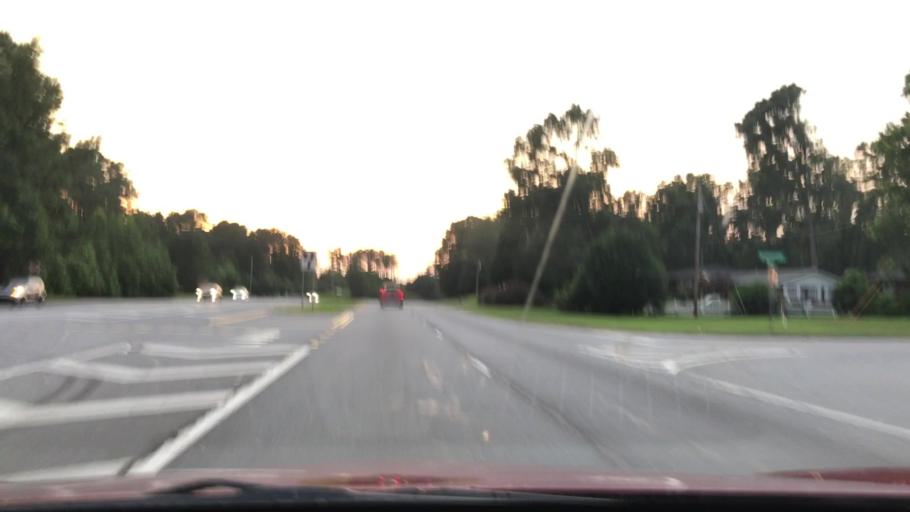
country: US
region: Georgia
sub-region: Gwinnett County
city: Lawrenceville
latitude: 33.9938
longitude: -83.9874
